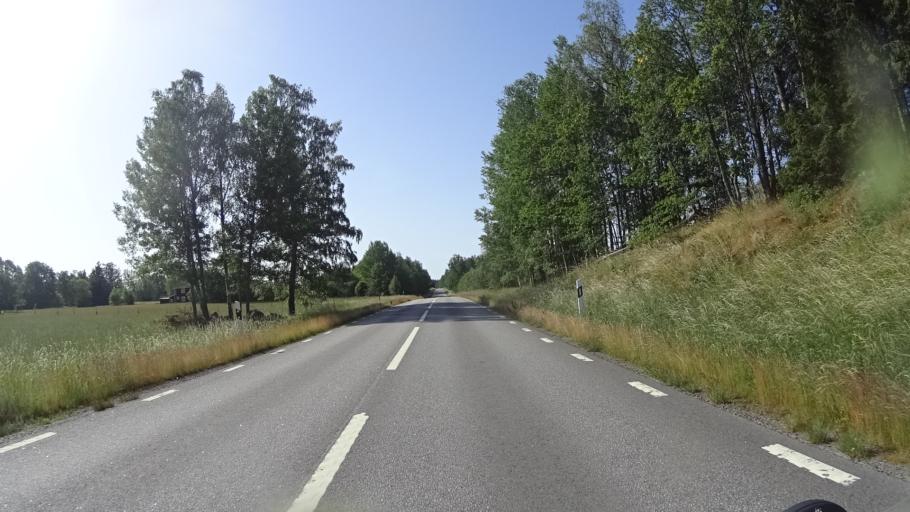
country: SE
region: OEstergoetland
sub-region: Atvidabergs Kommun
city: Atvidaberg
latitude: 58.1500
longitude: 16.0743
